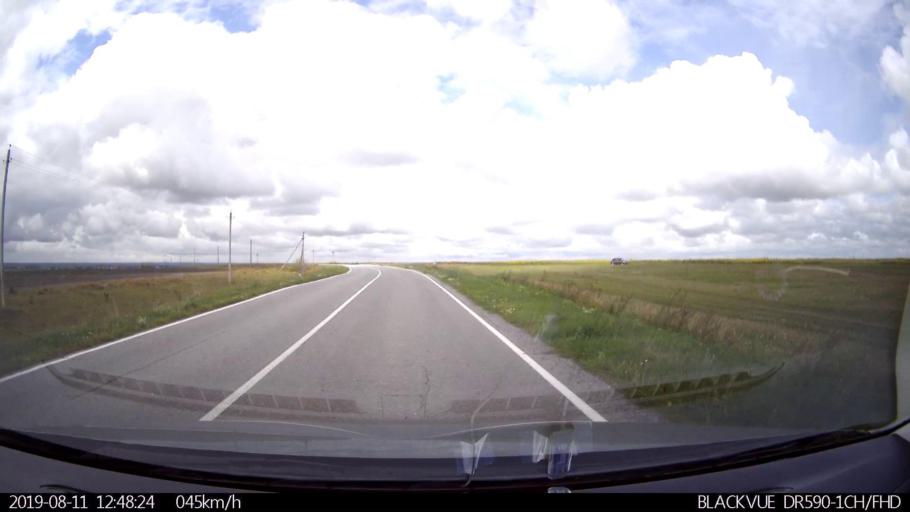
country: RU
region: Ulyanovsk
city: Ignatovka
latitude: 53.8737
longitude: 47.6995
